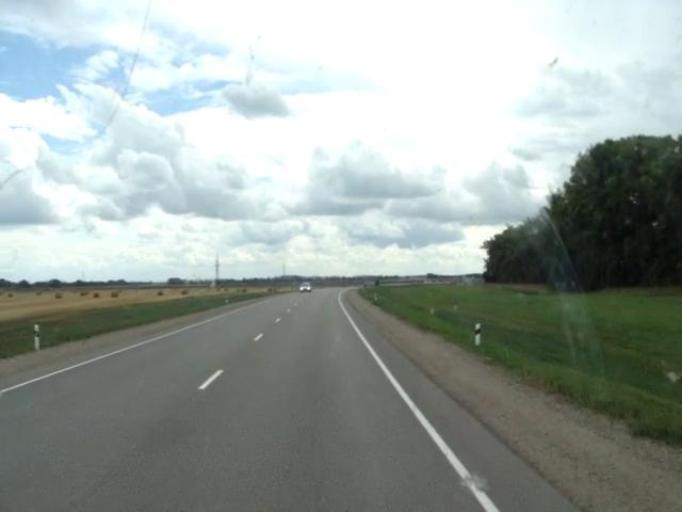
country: RU
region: Altai Krai
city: Shubenka
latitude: 52.6811
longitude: 85.0476
